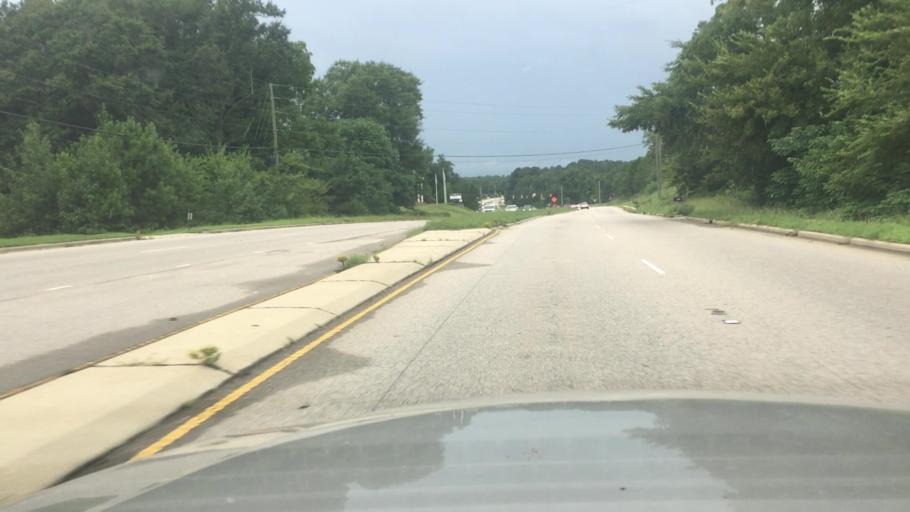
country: US
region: North Carolina
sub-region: Cumberland County
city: Hope Mills
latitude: 34.9993
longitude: -78.9732
